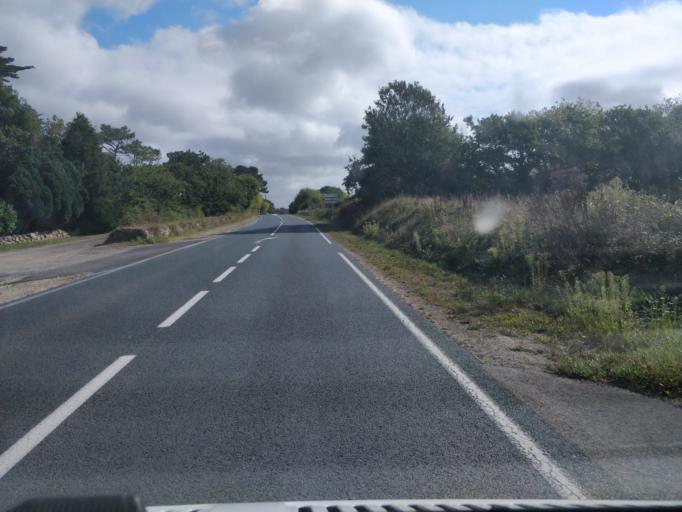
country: FR
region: Brittany
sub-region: Departement du Finistere
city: Landudec
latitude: 47.9990
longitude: -4.3574
